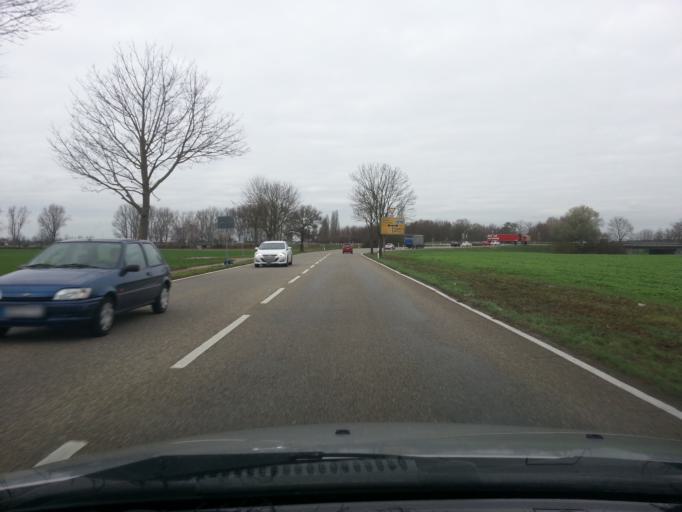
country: DE
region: Baden-Wuerttemberg
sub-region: Karlsruhe Region
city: Reilingen
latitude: 49.3022
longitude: 8.5662
